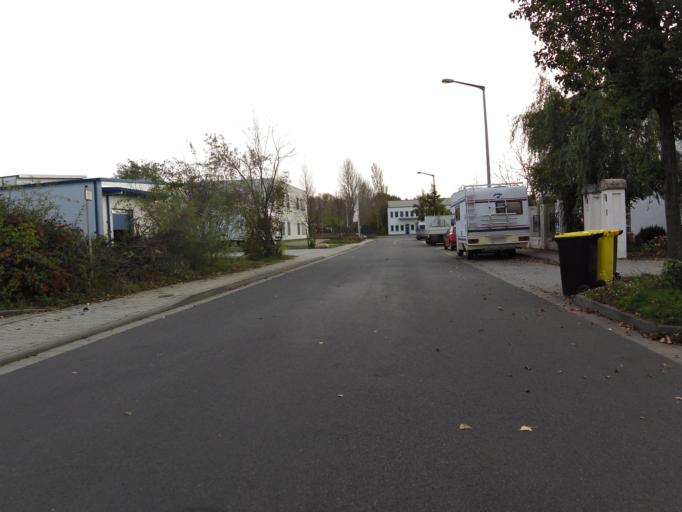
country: DE
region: Saxony
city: Taucha
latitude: 51.3666
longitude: 12.4272
